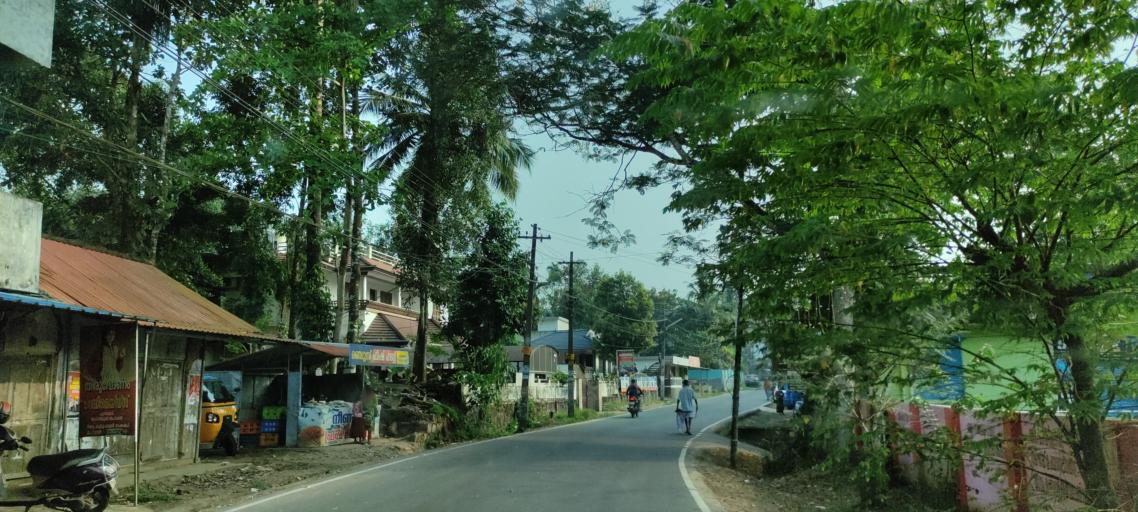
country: IN
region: Kerala
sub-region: Pattanamtitta
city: Adur
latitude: 9.1180
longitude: 76.7315
